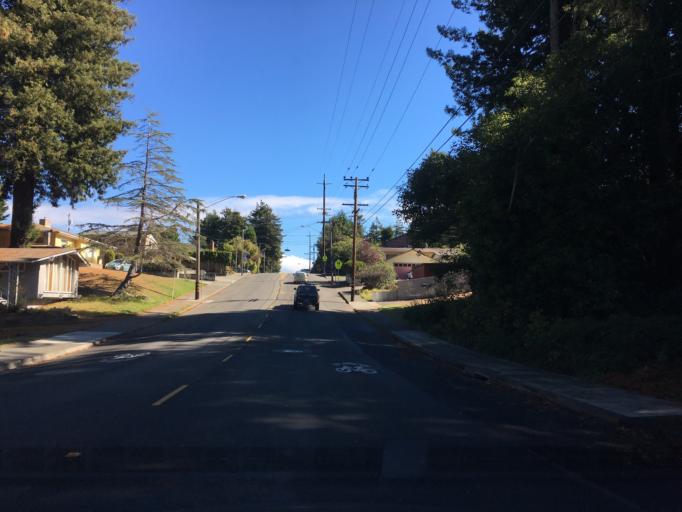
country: US
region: California
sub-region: Humboldt County
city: Cutten
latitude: 40.7805
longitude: -124.1435
